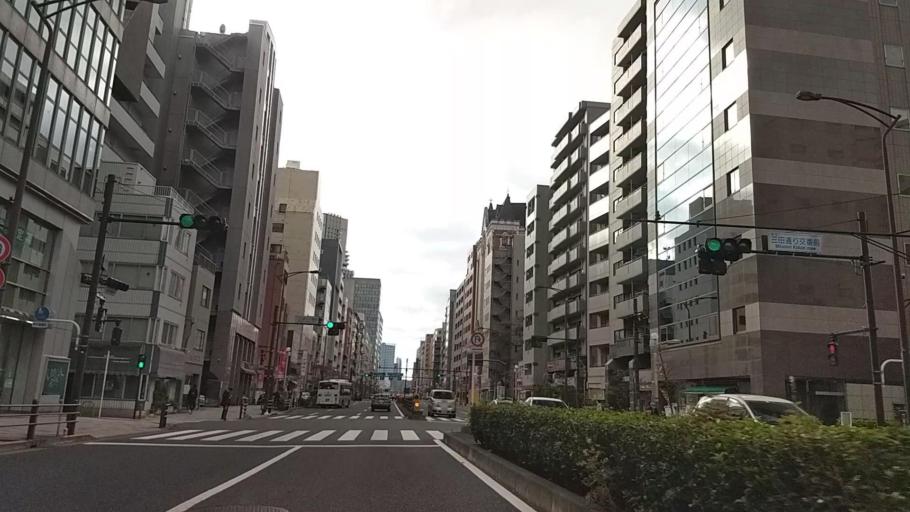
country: JP
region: Tokyo
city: Tokyo
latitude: 35.6505
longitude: 139.7449
